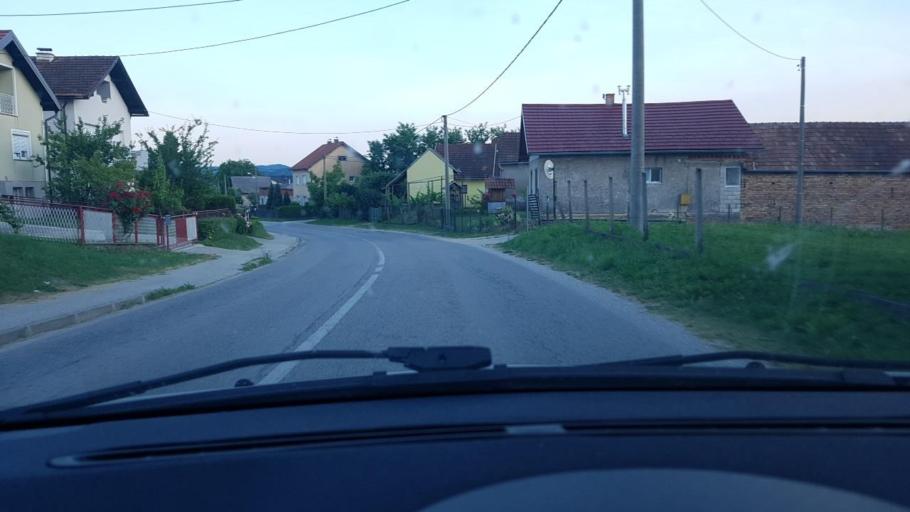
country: HR
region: Varazdinska
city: Remetinec
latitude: 46.1770
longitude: 16.3322
